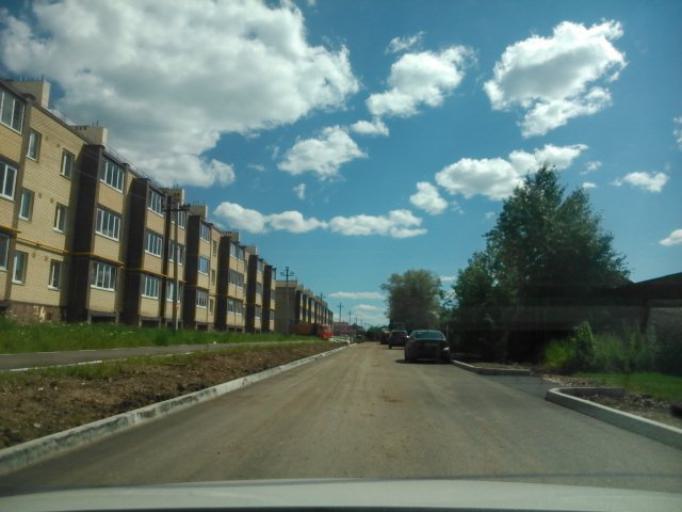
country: RU
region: Perm
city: Perm
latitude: 58.0016
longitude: 56.3354
